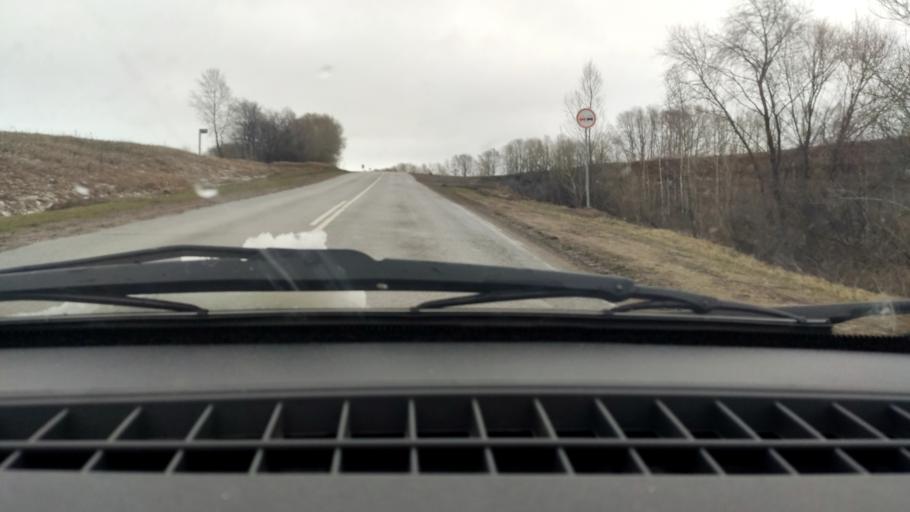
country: RU
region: Bashkortostan
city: Alekseyevka
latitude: 55.0670
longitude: 55.0935
